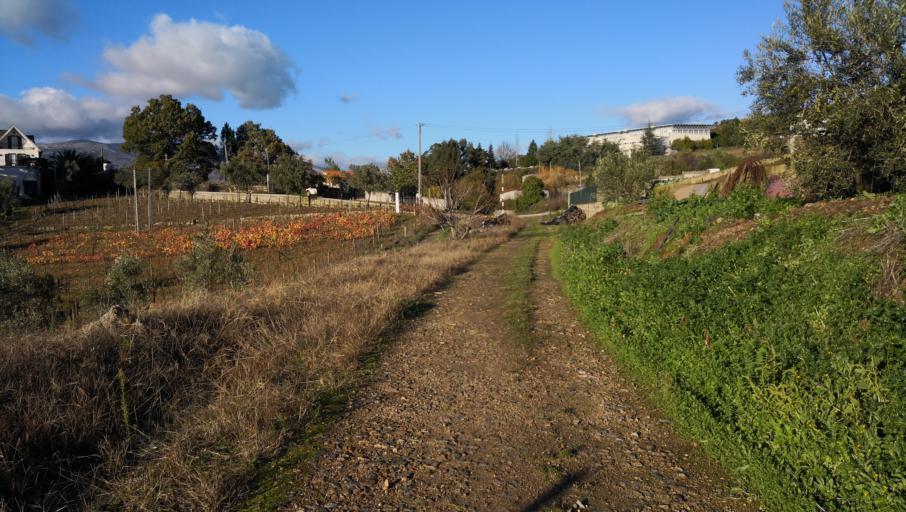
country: PT
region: Vila Real
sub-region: Vila Real
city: Vila Real
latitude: 41.2802
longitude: -7.7469
